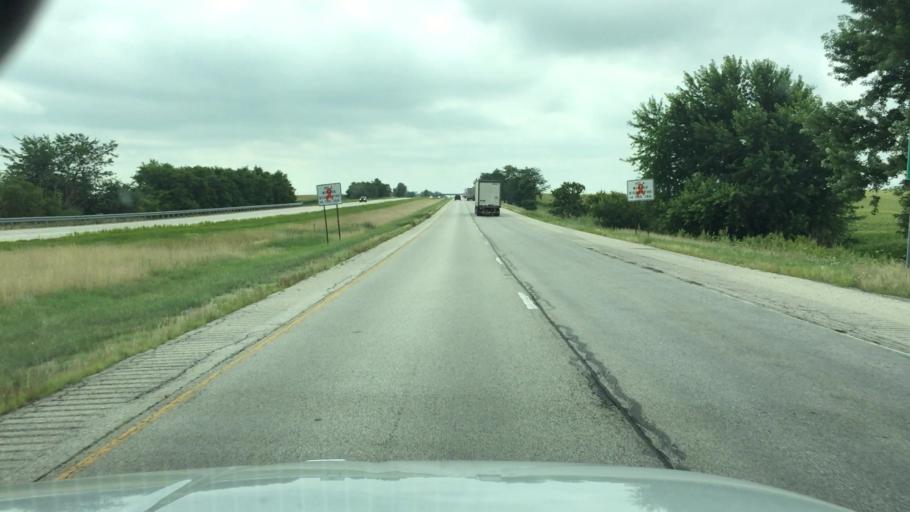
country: US
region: Illinois
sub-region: Knox County
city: Galesburg
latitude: 41.0345
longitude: -90.3346
